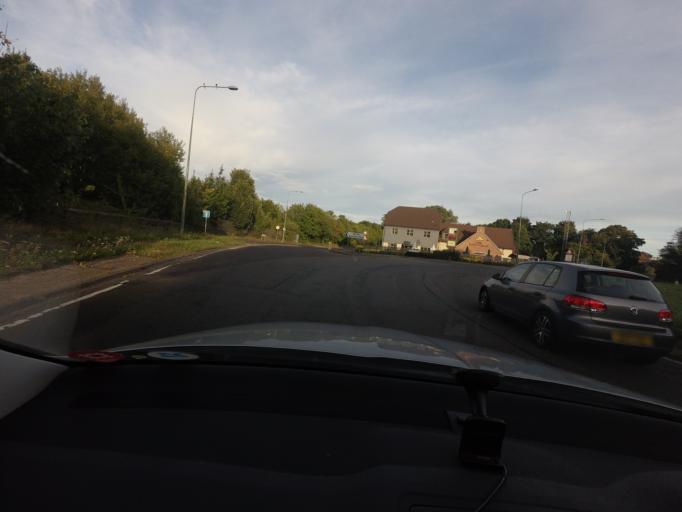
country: GB
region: England
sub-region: Kent
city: Aylesford
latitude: 51.2911
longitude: 0.4873
